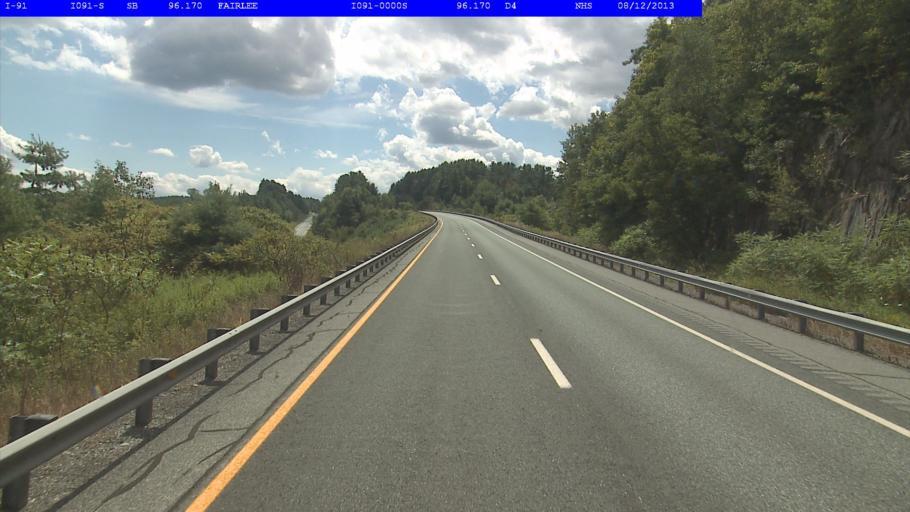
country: US
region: New Hampshire
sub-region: Grafton County
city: Orford
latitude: 43.9642
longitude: -72.1284
